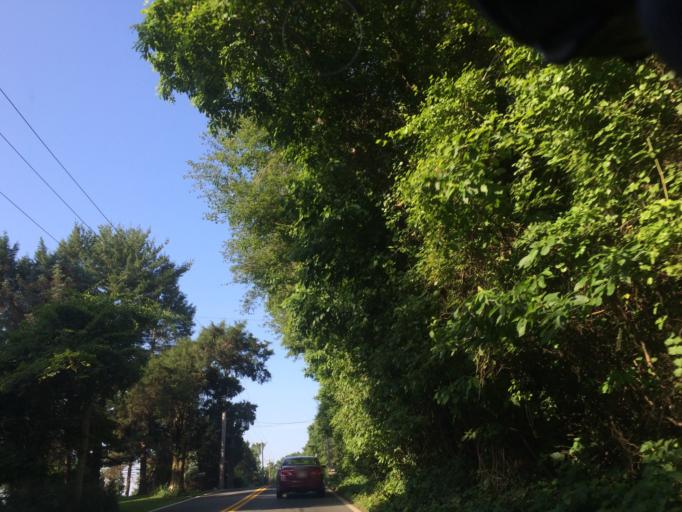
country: US
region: Maryland
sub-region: Montgomery County
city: Ashton-Sandy Spring
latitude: 39.1986
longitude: -77.0244
